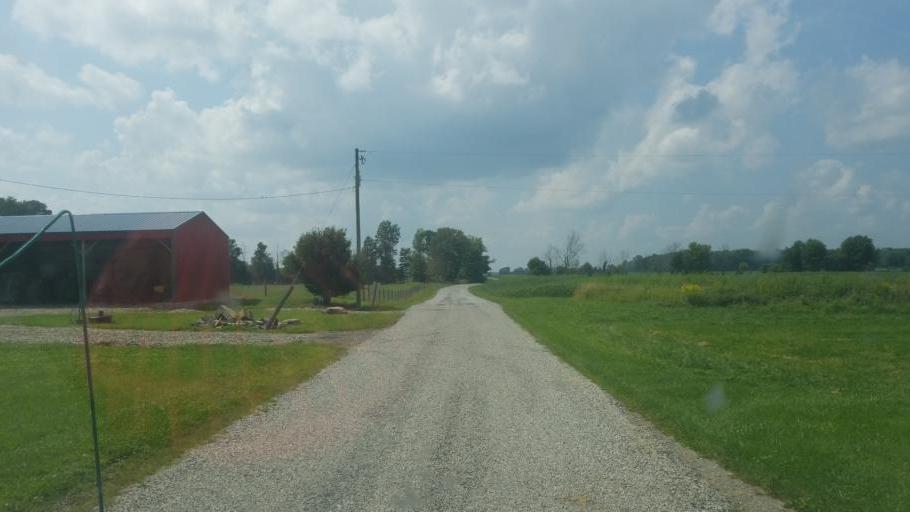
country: US
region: Ohio
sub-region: Huron County
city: New London
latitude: 40.9868
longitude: -82.4174
